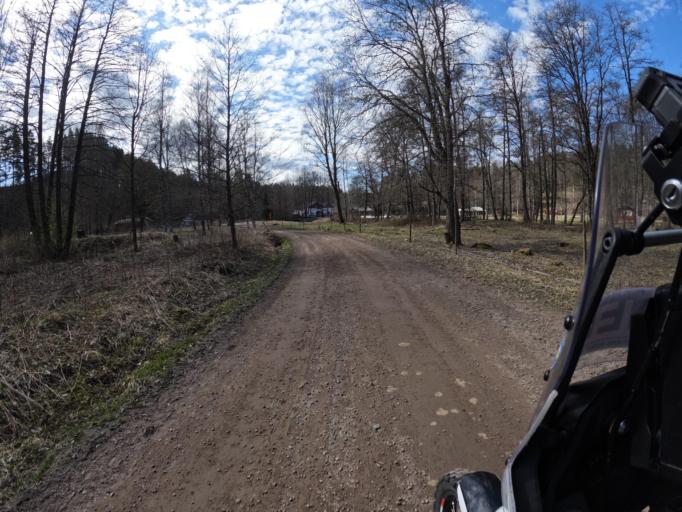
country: SE
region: Joenkoeping
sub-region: Mullsjo Kommun
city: Mullsjoe
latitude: 57.9964
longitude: 13.8470
